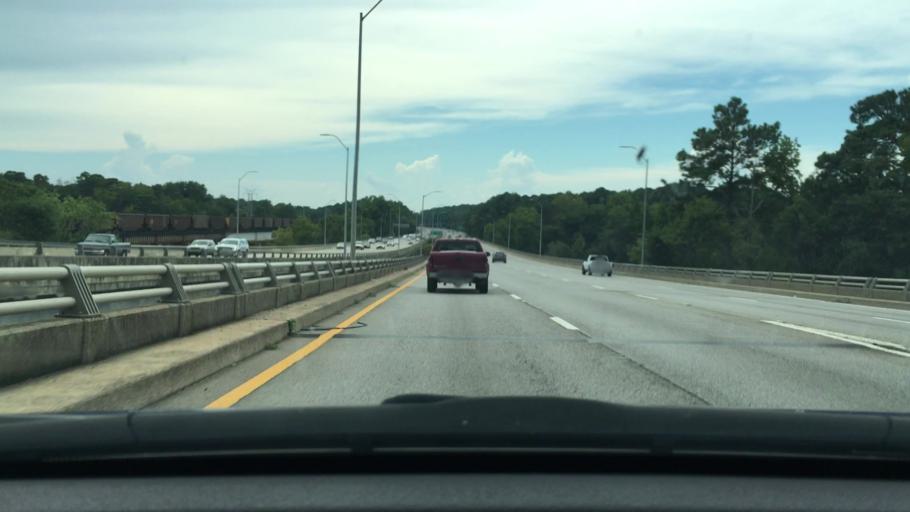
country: US
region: South Carolina
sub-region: Lexington County
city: West Columbia
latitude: 34.0089
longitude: -81.0580
